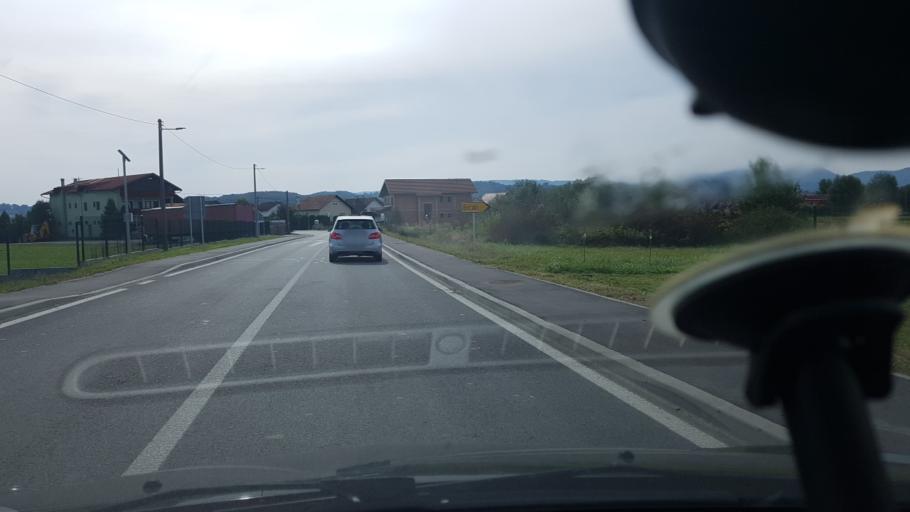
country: HR
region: Krapinsko-Zagorska
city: Marija Bistrica
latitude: 46.0548
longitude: 16.1665
